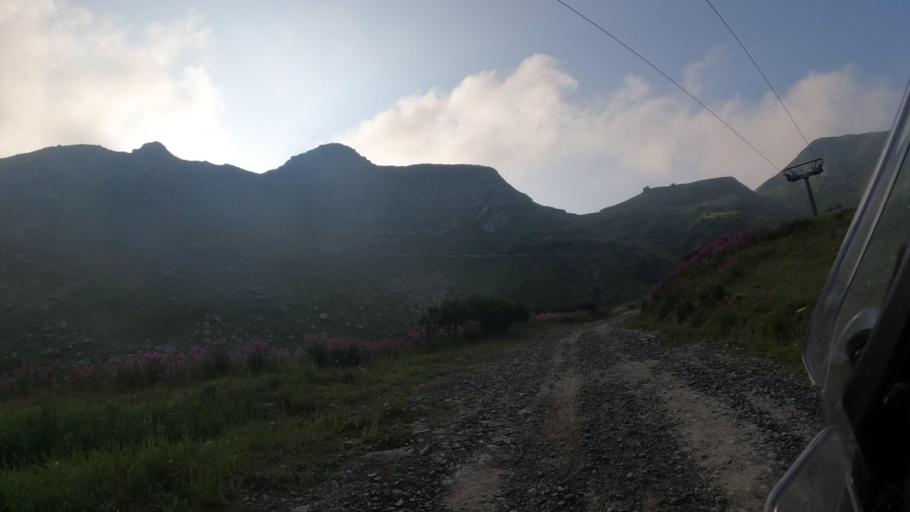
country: IT
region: Piedmont
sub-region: Provincia di Cuneo
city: Limone Piemonte
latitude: 44.1576
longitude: 7.5948
